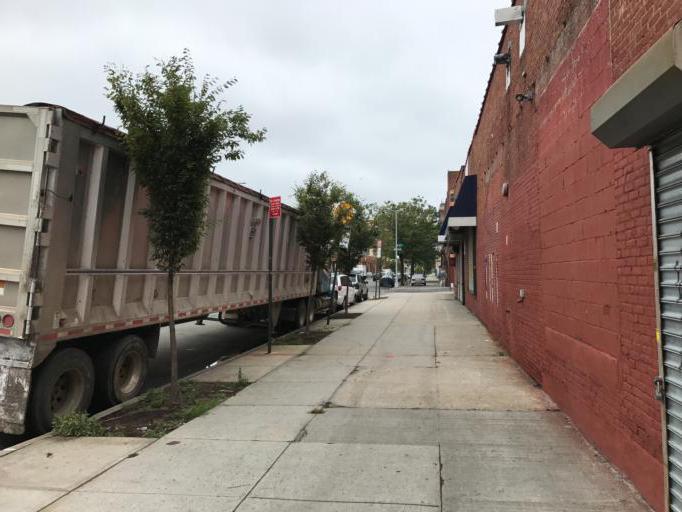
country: US
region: New York
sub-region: Kings County
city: Bensonhurst
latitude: 40.6503
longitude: -74.0155
